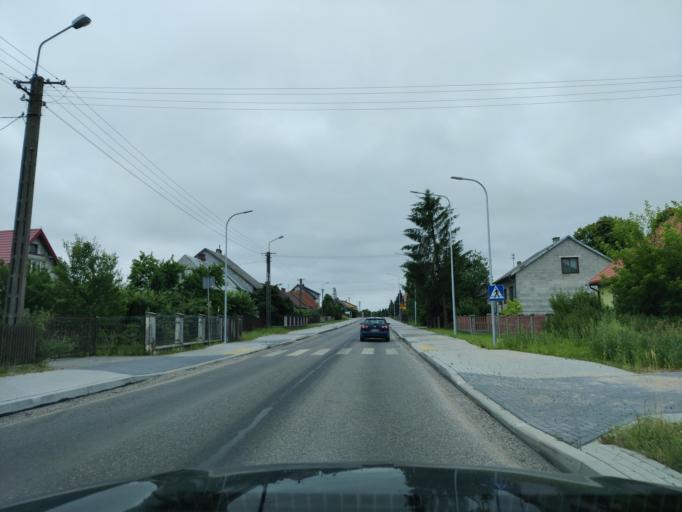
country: PL
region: Warmian-Masurian Voivodeship
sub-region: Powiat szczycienski
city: Rozogi
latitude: 53.4397
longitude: 21.3711
